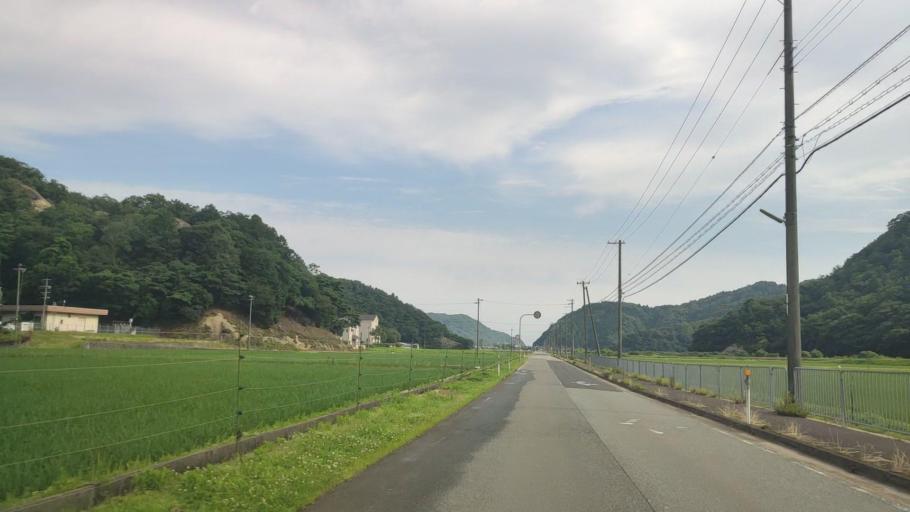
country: JP
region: Hyogo
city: Toyooka
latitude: 35.6236
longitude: 134.8412
